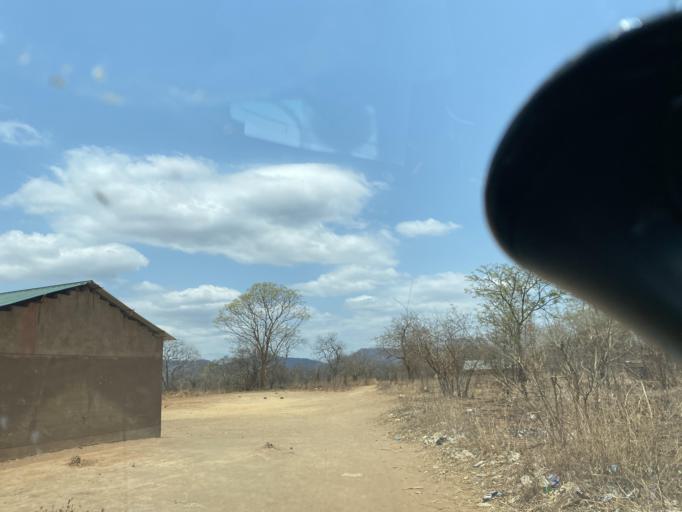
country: ZM
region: Lusaka
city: Luangwa
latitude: -15.1869
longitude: 29.7300
